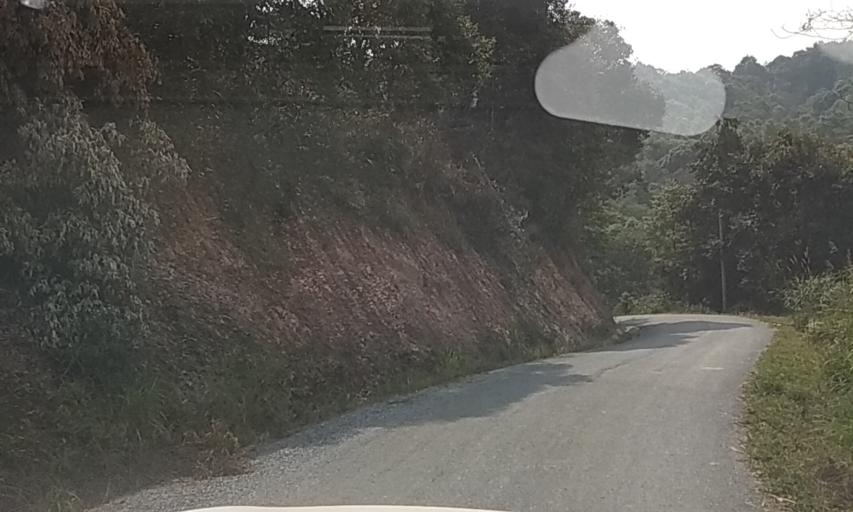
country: TH
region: Nan
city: Chaloem Phra Kiat
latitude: 20.0521
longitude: 101.0754
